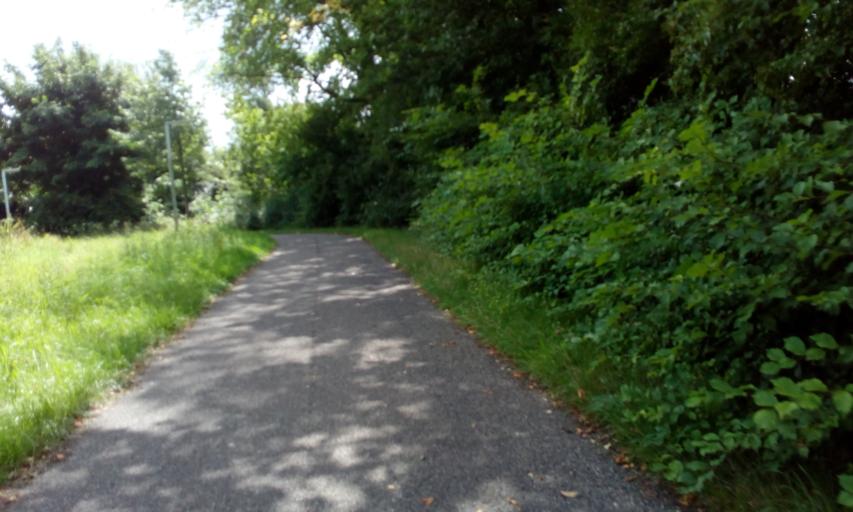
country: NL
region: South Holland
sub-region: Gemeente Delft
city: Delft
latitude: 52.0041
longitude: 4.3401
